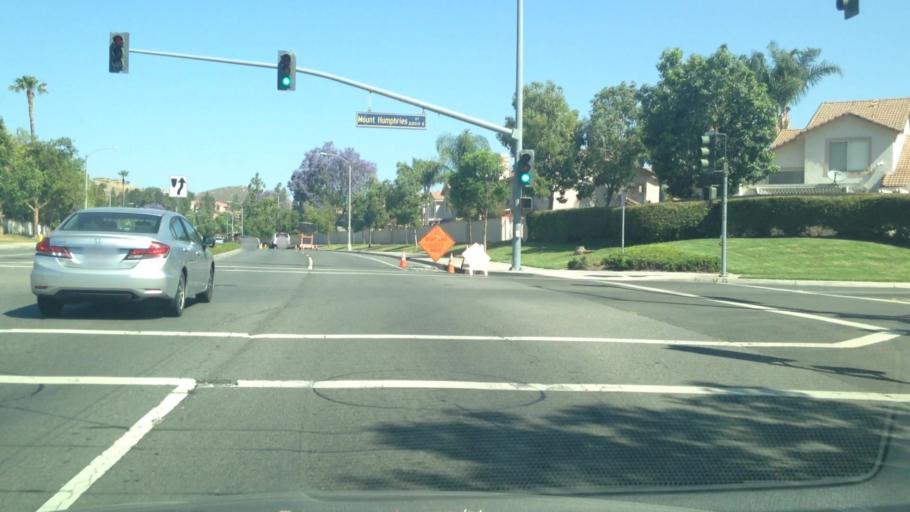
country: US
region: California
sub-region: Riverside County
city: Home Gardens
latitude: 33.8950
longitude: -117.5250
